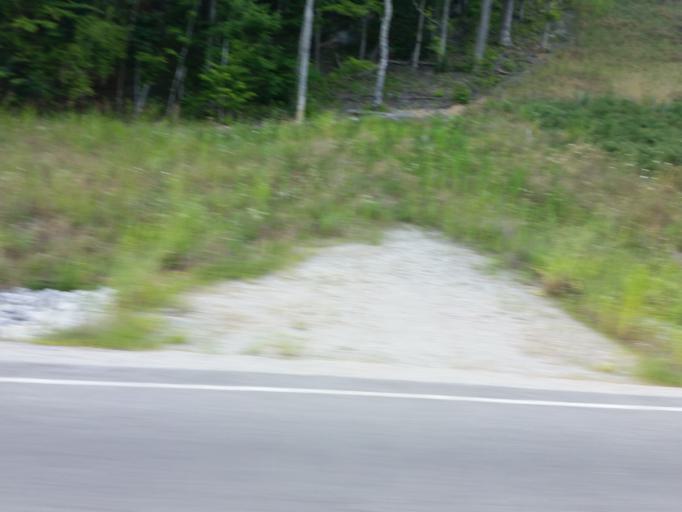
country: US
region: Tennessee
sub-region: Maury County
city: Mount Pleasant
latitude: 35.5643
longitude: -87.3756
